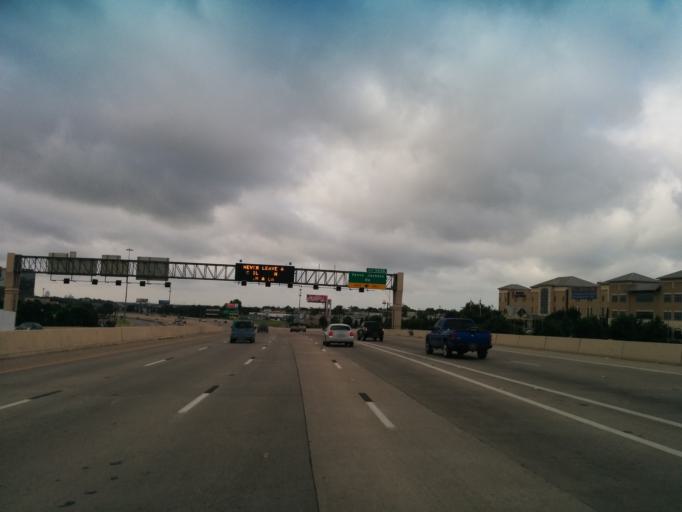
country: US
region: Texas
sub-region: Bexar County
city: Balcones Heights
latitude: 29.4923
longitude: -98.5469
